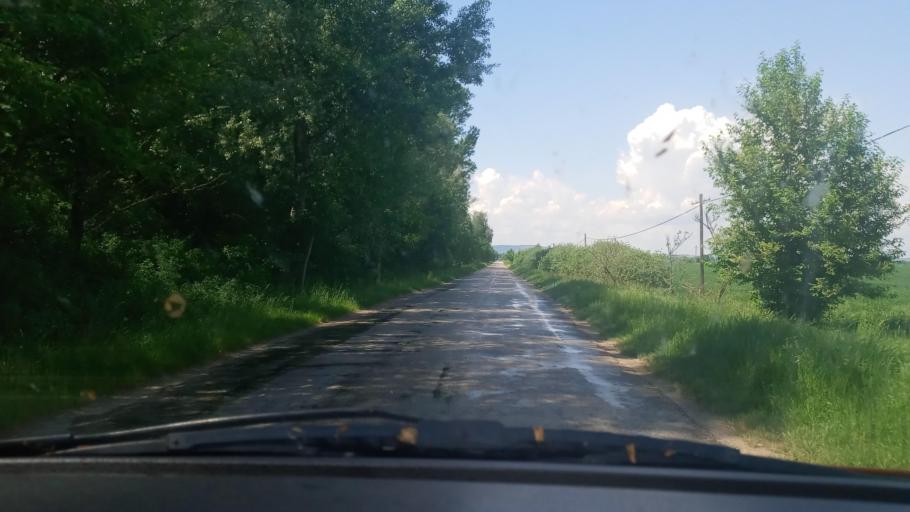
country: HU
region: Baranya
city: Siklos
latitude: 45.7987
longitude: 18.3487
